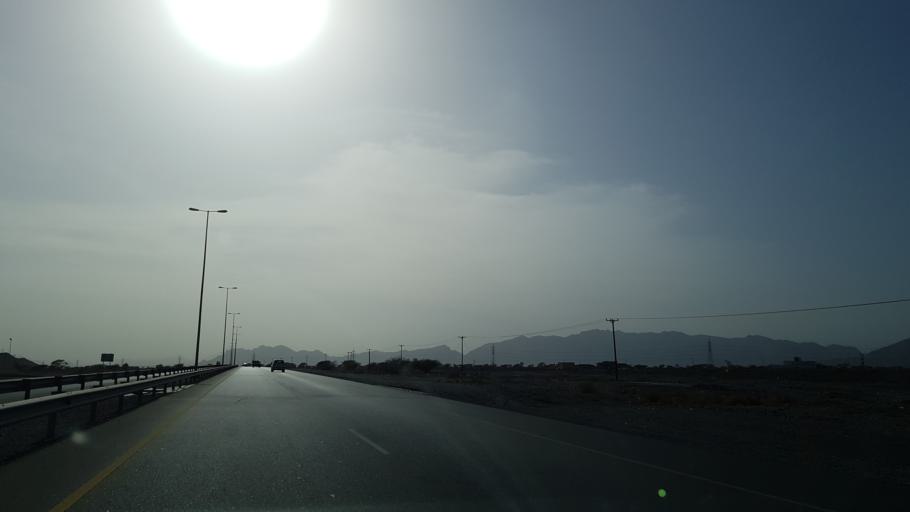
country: OM
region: Muhafazat ad Dakhiliyah
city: Izki
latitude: 22.8915
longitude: 57.6637
